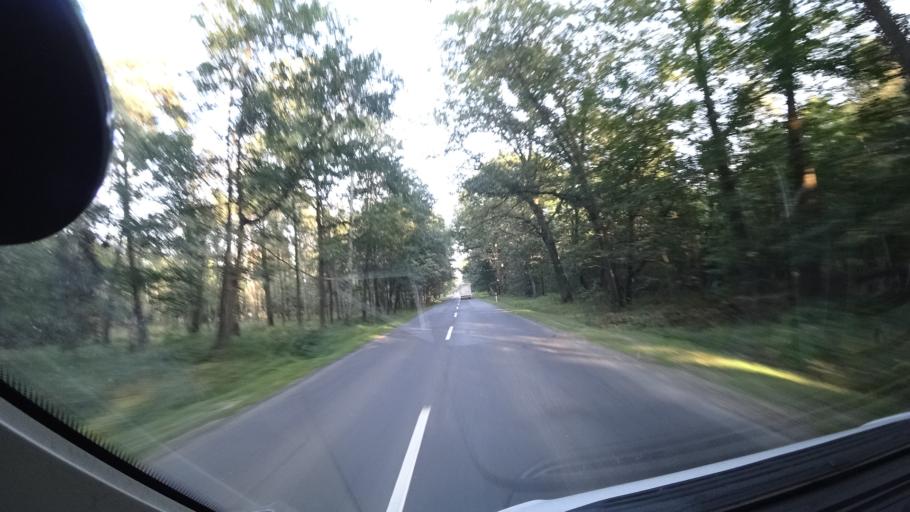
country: PL
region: Silesian Voivodeship
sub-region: Powiat gliwicki
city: Rudziniec
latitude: 50.2735
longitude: 18.3911
